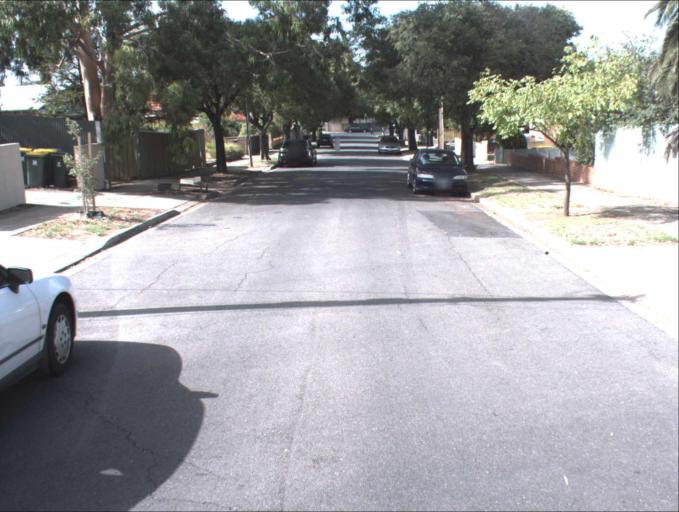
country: AU
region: South Australia
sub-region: Port Adelaide Enfield
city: Blair Athol
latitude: -34.8672
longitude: 138.6000
